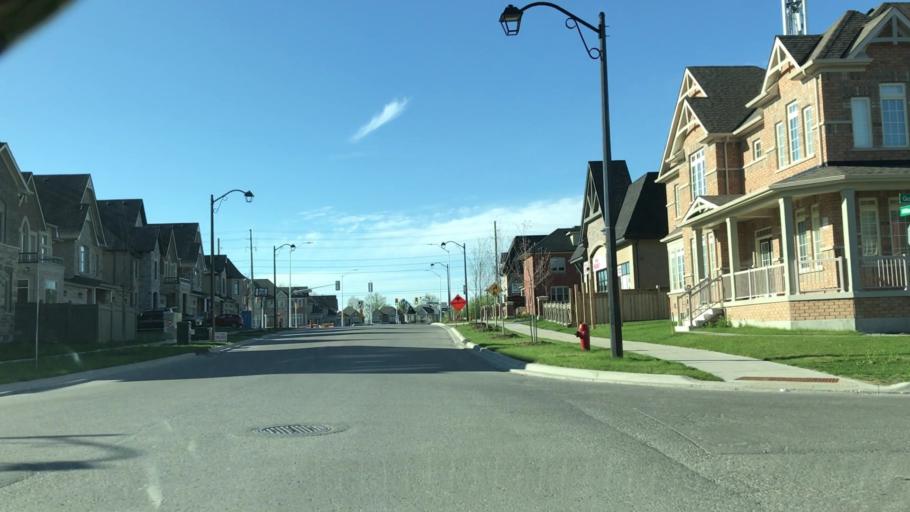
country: CA
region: Ontario
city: Newmarket
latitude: 44.0259
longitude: -79.4303
